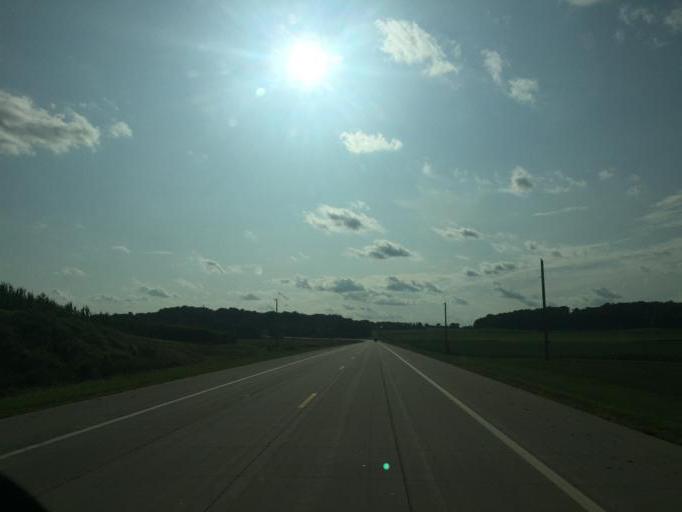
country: US
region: Minnesota
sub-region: Olmsted County
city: Rochester
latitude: 43.9964
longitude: -92.5421
